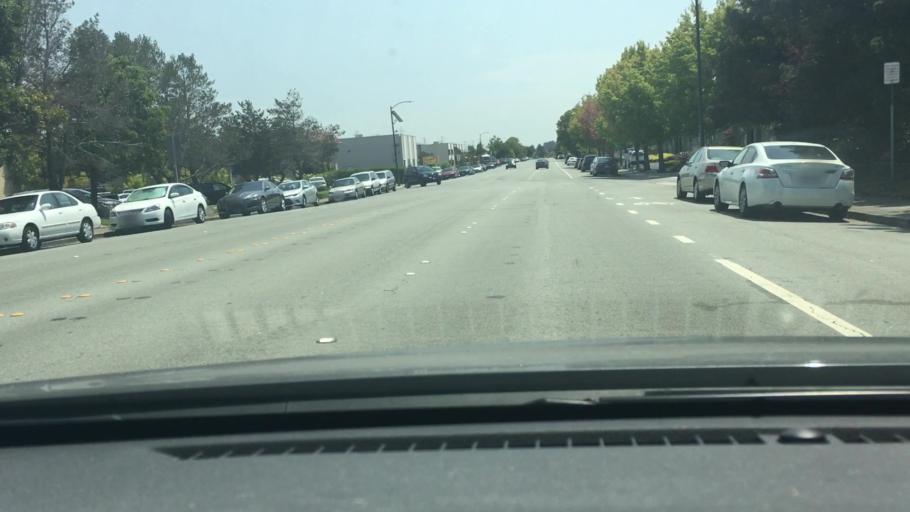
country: US
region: California
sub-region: San Mateo County
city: Millbrae
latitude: 37.5966
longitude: -122.3774
